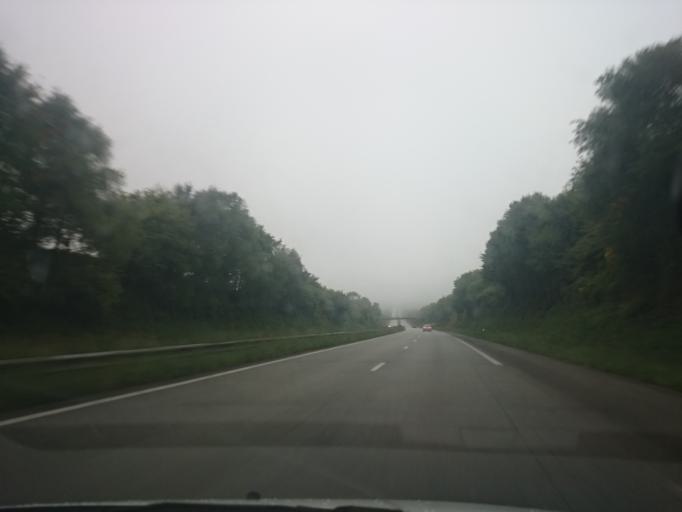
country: FR
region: Brittany
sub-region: Departement du Finistere
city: Briec
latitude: 48.1297
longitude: -4.0237
